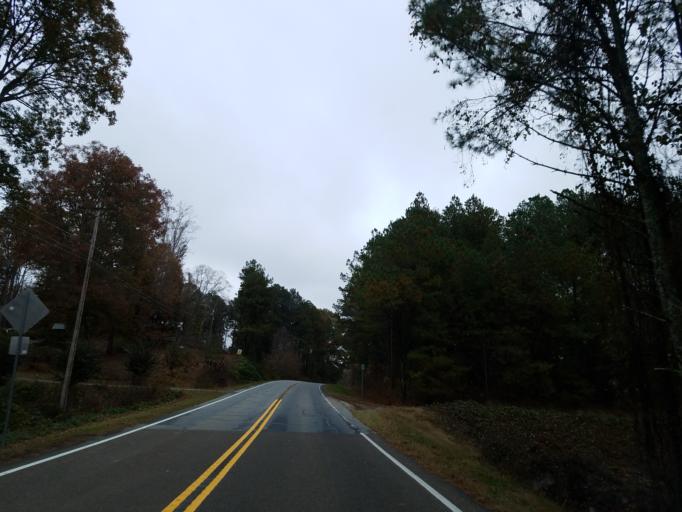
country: US
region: Georgia
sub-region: Cherokee County
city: Canton
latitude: 34.2819
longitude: -84.5669
